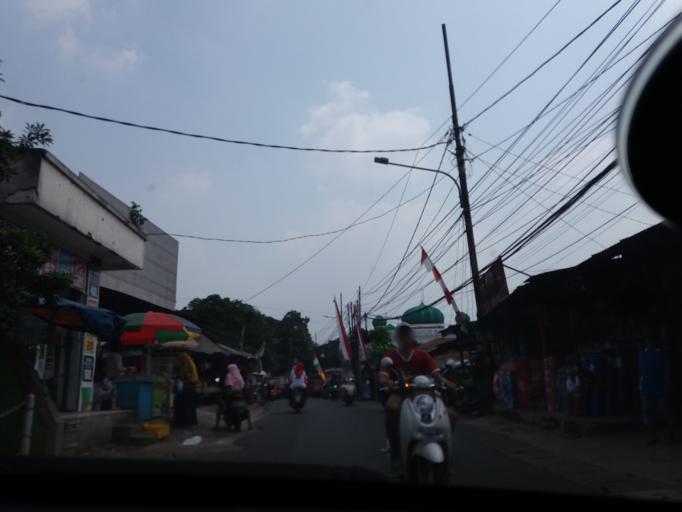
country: ID
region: West Java
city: Depok
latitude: -6.3311
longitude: 106.8327
